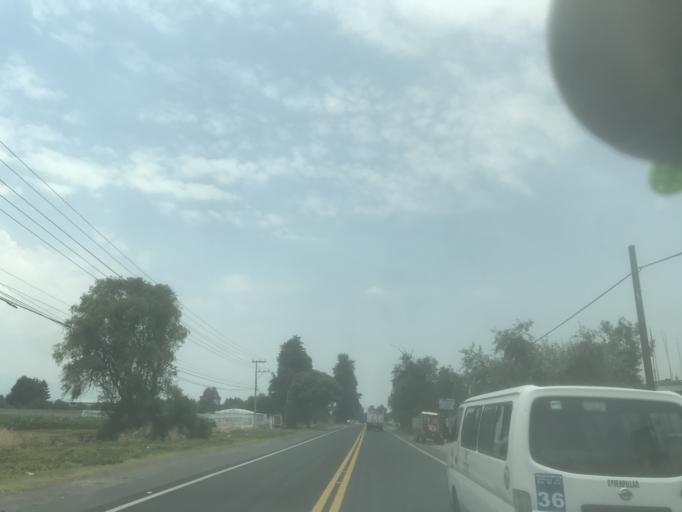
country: MX
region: Mexico
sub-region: Amecameca
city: San Diego Huehuecalco
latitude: 19.0885
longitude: -98.7820
